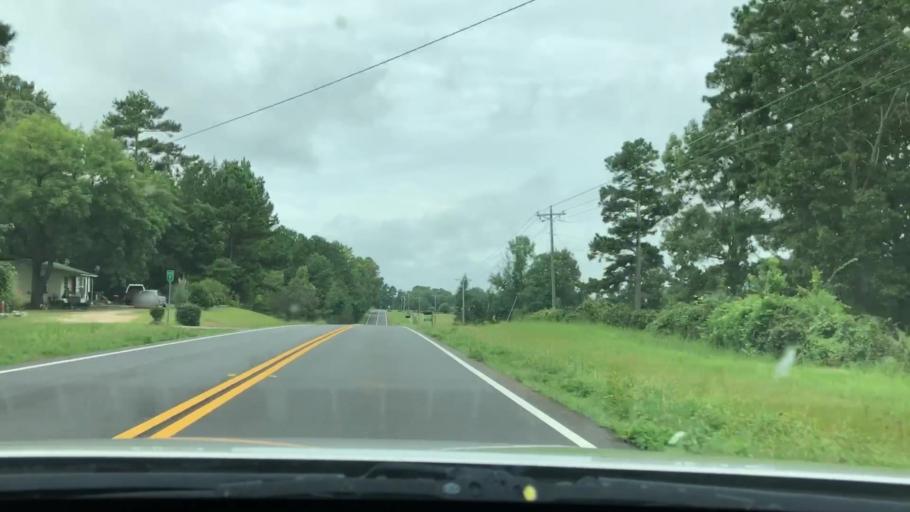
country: US
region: Georgia
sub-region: Upson County
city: Hannahs Mill
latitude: 33.0130
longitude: -84.4275
